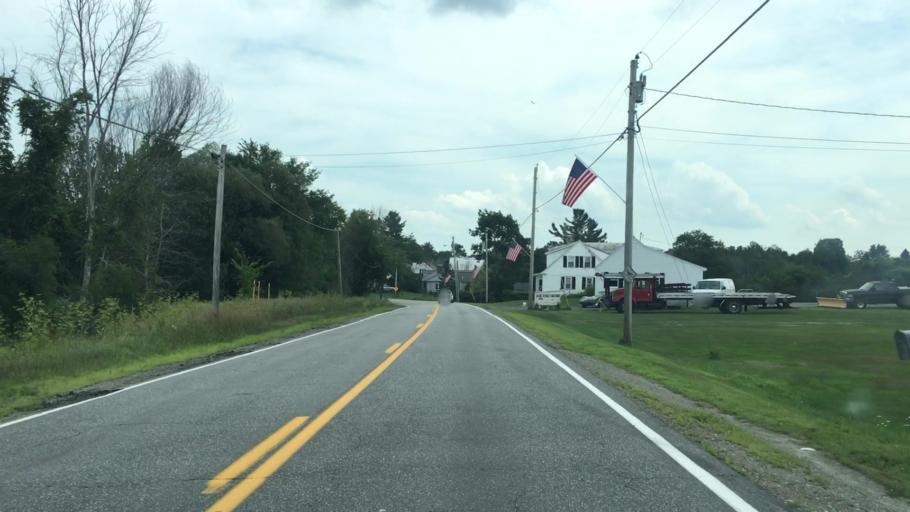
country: US
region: Maine
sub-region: Kennebec County
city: Vassalboro
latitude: 44.4531
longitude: -69.6085
